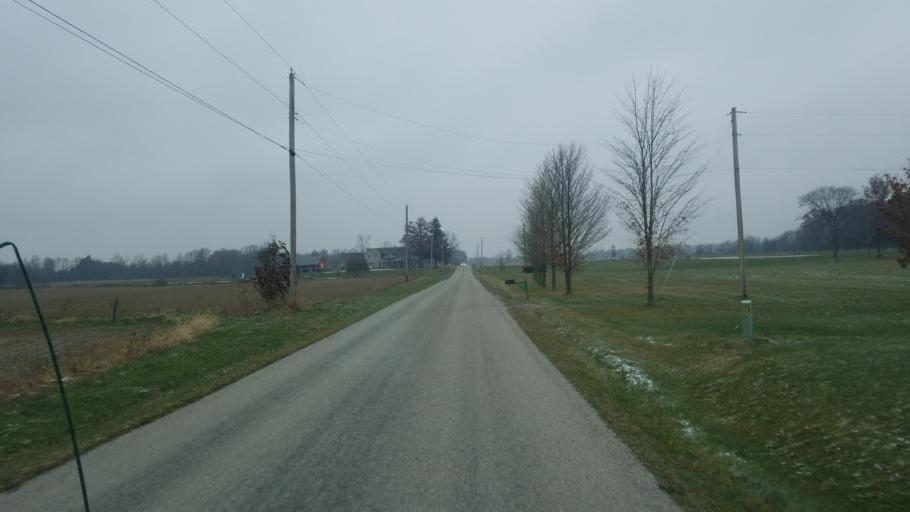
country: US
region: Ohio
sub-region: Huron County
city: New London
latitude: 41.0206
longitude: -82.3256
